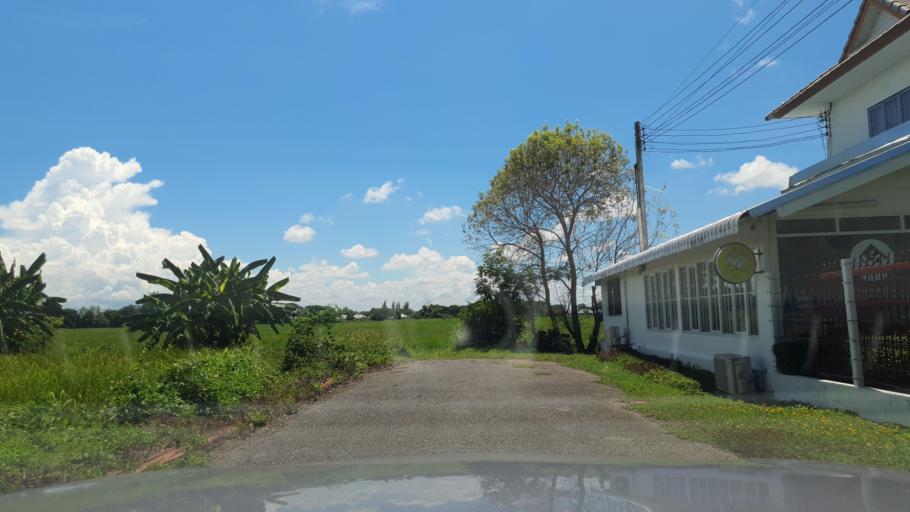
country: TH
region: Chiang Mai
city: San Kamphaeng
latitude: 18.7536
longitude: 99.0968
